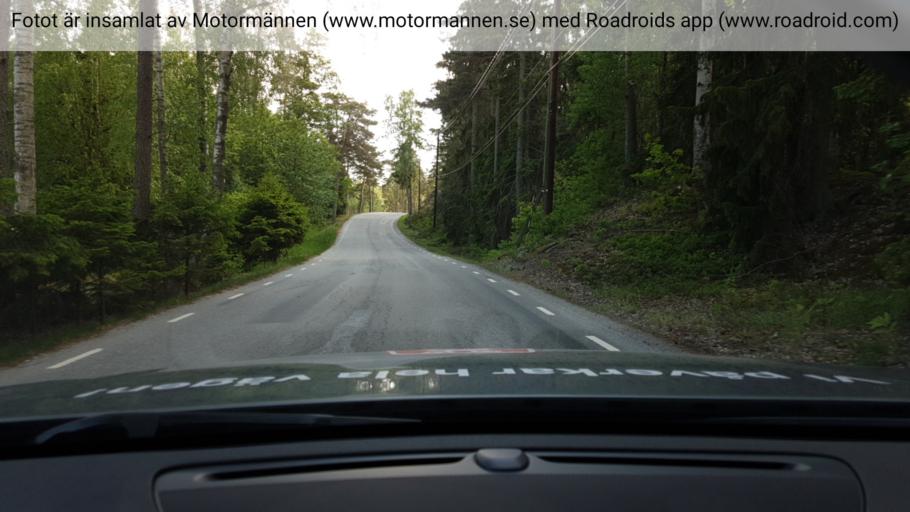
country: SE
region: Stockholm
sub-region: Varmdo Kommun
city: Mortnas
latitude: 59.2625
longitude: 18.4332
